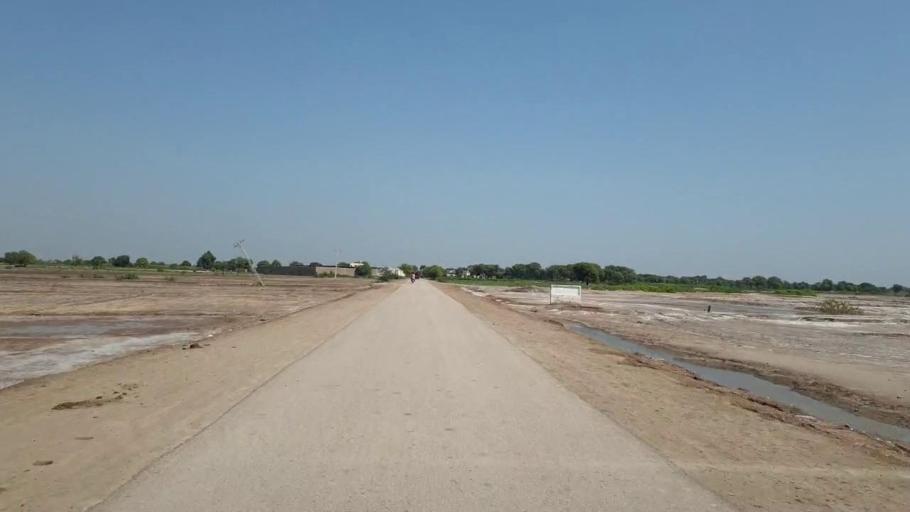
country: PK
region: Sindh
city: Hyderabad
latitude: 25.4476
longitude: 68.4131
